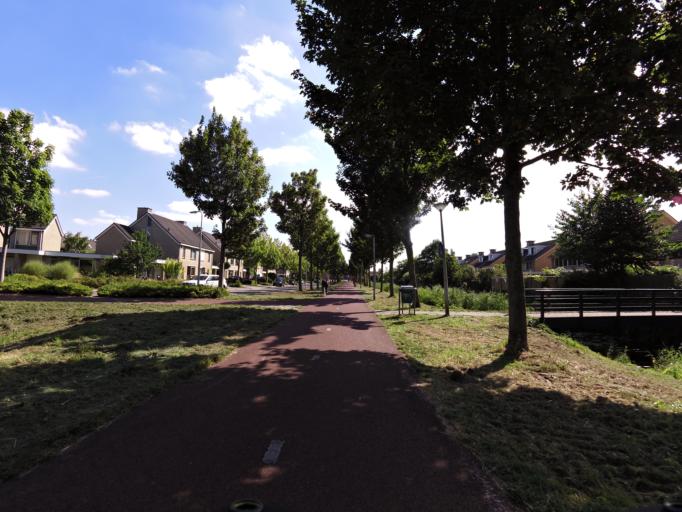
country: NL
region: South Holland
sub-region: Gemeente Barendrecht
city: Barendrecht
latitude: 51.8615
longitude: 4.5289
